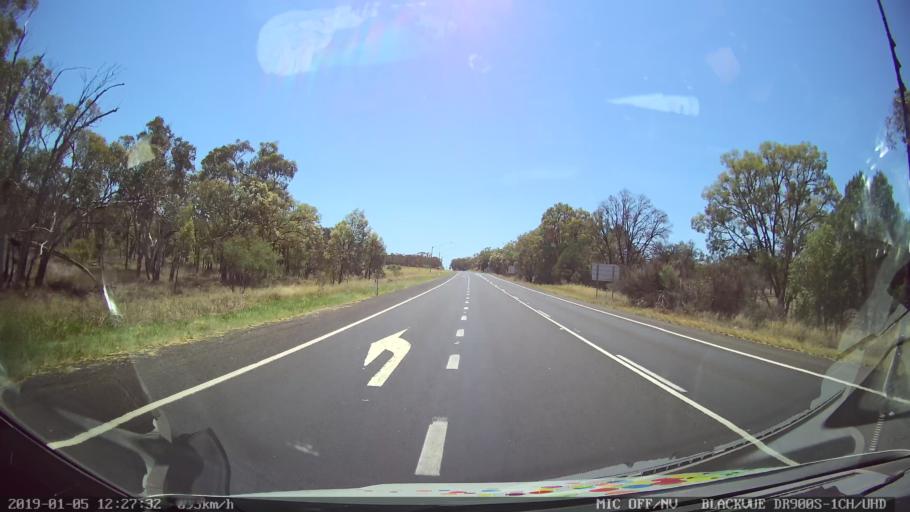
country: AU
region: New South Wales
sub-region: Warrumbungle Shire
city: Coonabarabran
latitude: -31.2468
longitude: 149.3109
